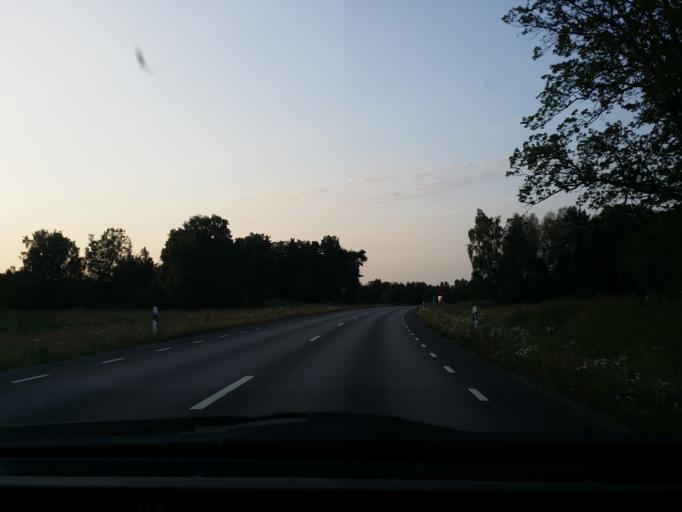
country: SE
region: Vaestmanland
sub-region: Vasteras
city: Tillberga
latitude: 59.5979
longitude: 16.6653
